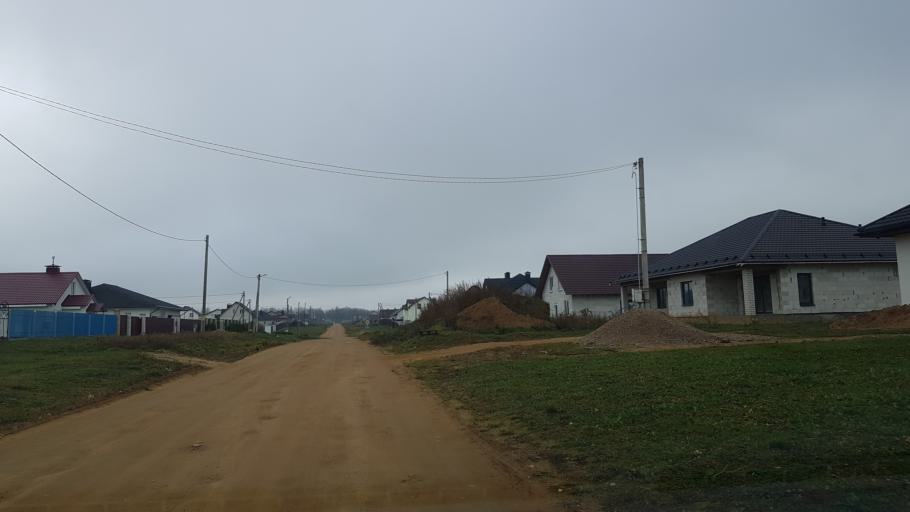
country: BY
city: Fanipol
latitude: 53.7319
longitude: 27.3207
